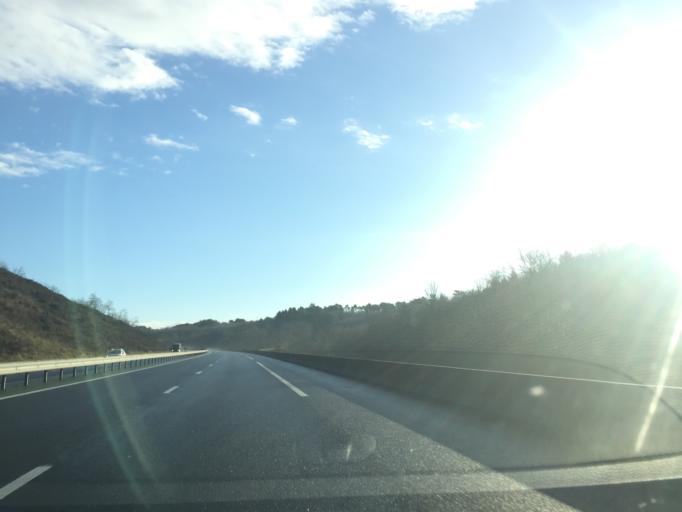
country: FR
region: Limousin
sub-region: Departement de la Correze
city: Cublac
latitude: 45.1660
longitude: 1.2743
